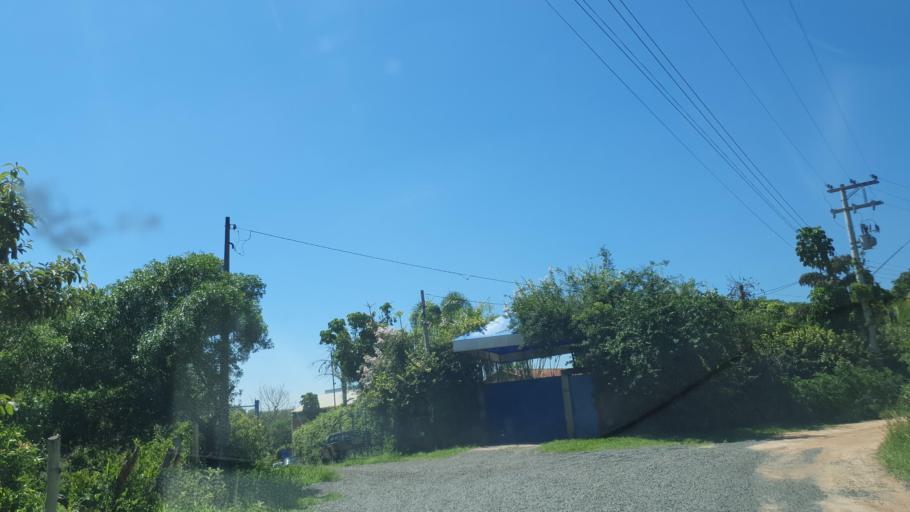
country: BR
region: Sao Paulo
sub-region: Sorocaba
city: Sorocaba
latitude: -23.4140
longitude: -47.4749
